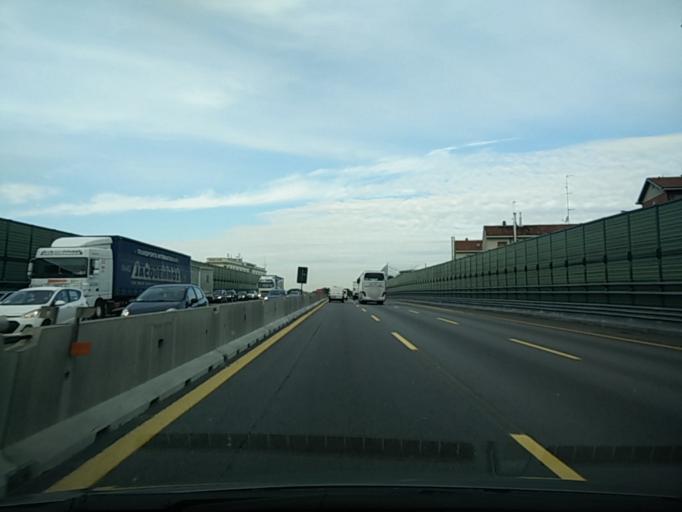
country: IT
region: Lombardy
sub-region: Citta metropolitana di Milano
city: Cinisello Balsamo
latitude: 45.5495
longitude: 9.2236
